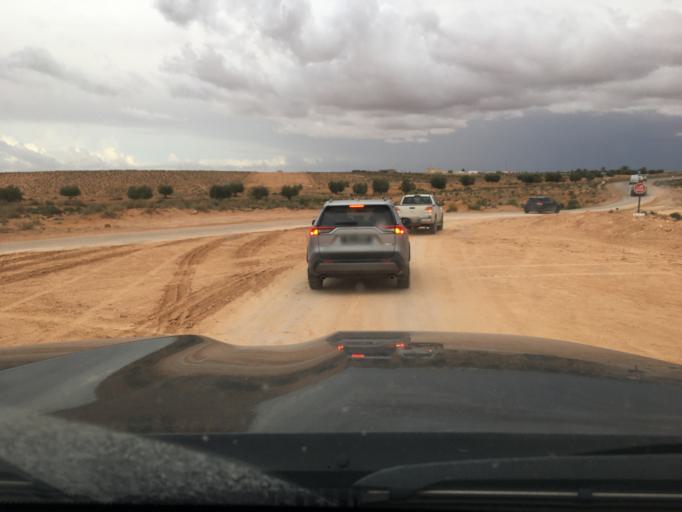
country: TN
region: Madanin
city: Medenine
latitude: 33.2868
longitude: 10.6003
